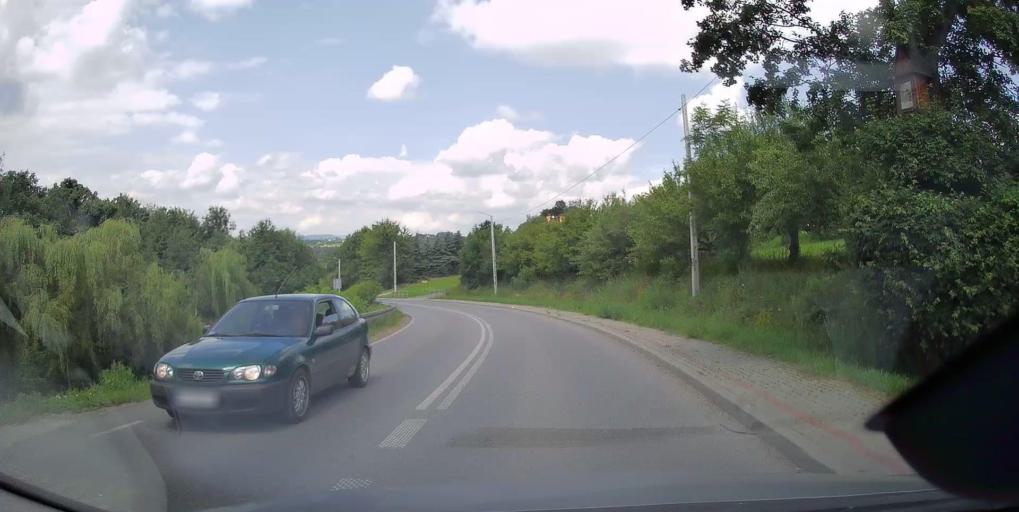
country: PL
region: Lesser Poland Voivodeship
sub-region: Powiat nowosadecki
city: Nowy Sacz
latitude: 49.6667
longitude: 20.7531
